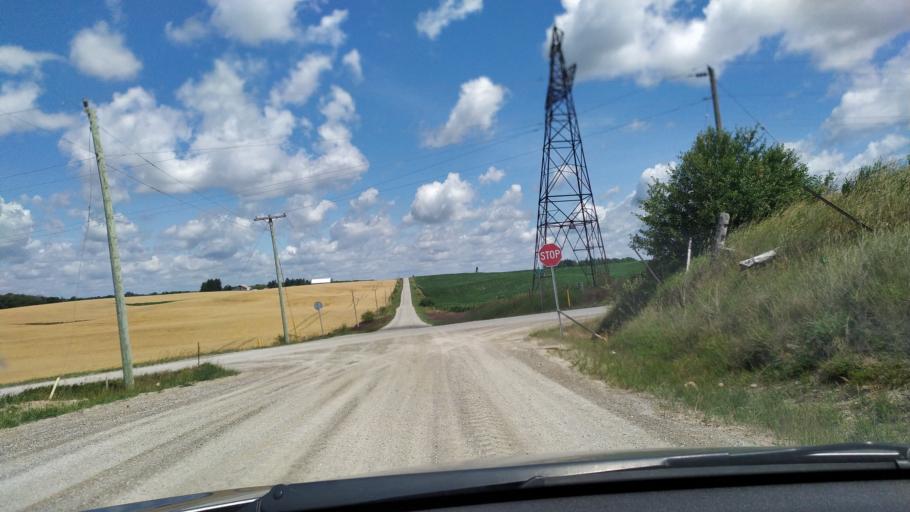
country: CA
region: Ontario
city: Stratford
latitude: 43.3871
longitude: -80.7619
